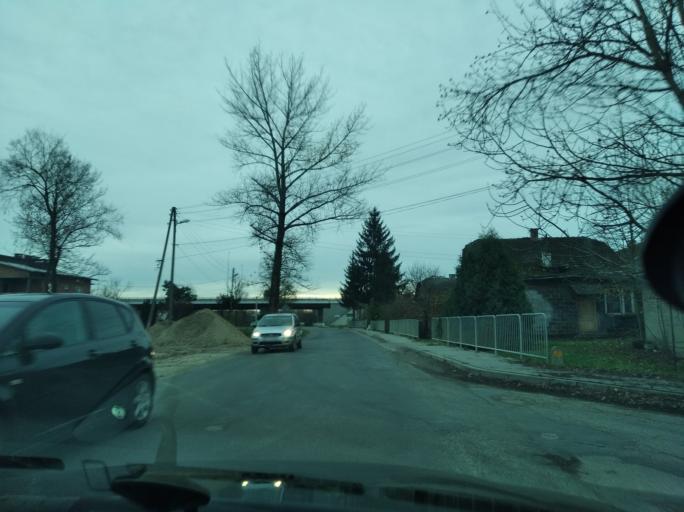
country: PL
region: Subcarpathian Voivodeship
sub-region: Powiat lancucki
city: Czarna
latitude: 50.0921
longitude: 22.1841
